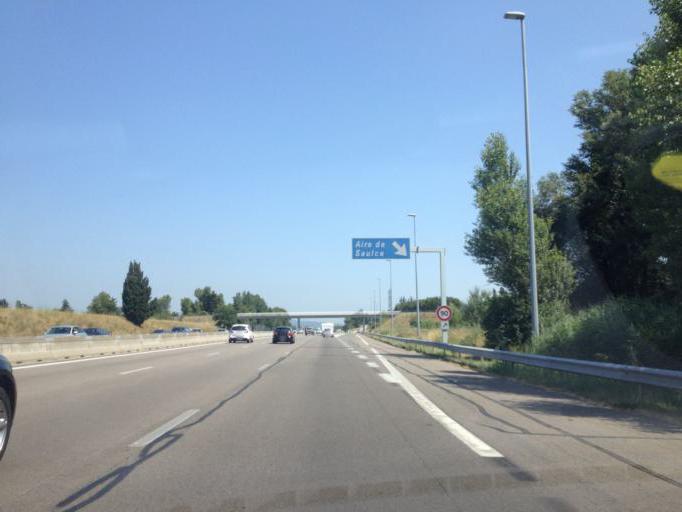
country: FR
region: Rhone-Alpes
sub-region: Departement de la Drome
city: Saulce-sur-Rhone
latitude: 44.7168
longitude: 4.7854
